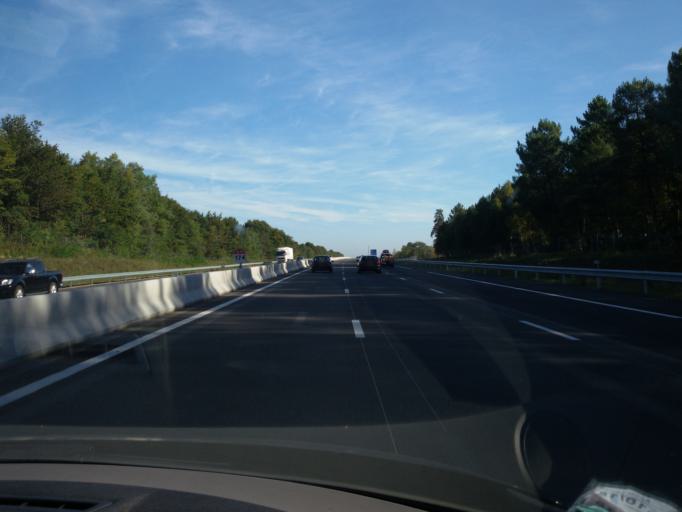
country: FR
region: Centre
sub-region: Departement du Loir-et-Cher
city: Theillay
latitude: 47.2698
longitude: 2.0424
